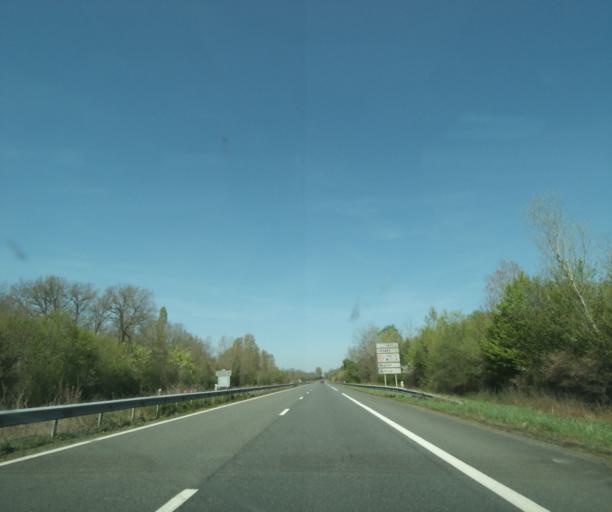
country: FR
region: Bourgogne
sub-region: Departement de la Nievre
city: La Charite-sur-Loire
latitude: 47.2210
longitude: 3.0042
